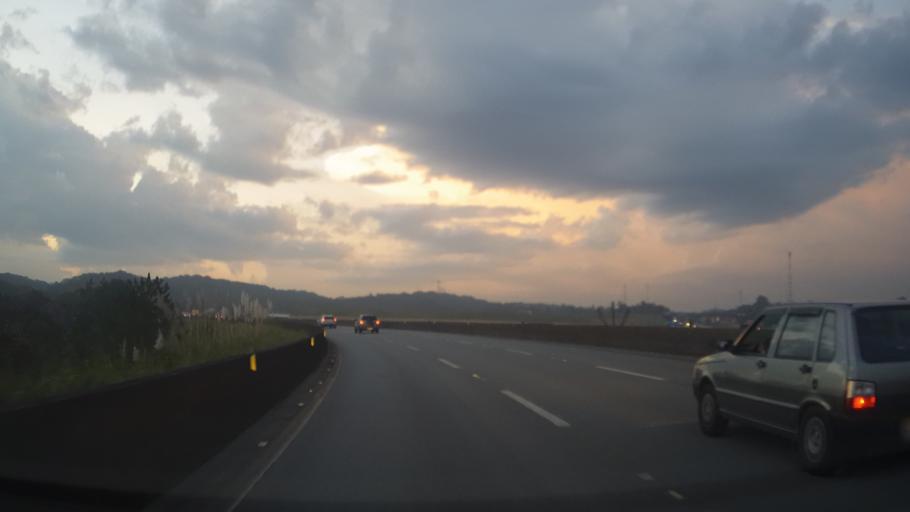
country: BR
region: Sao Paulo
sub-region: Cubatao
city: Cubatao
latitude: -23.8986
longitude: -46.5630
